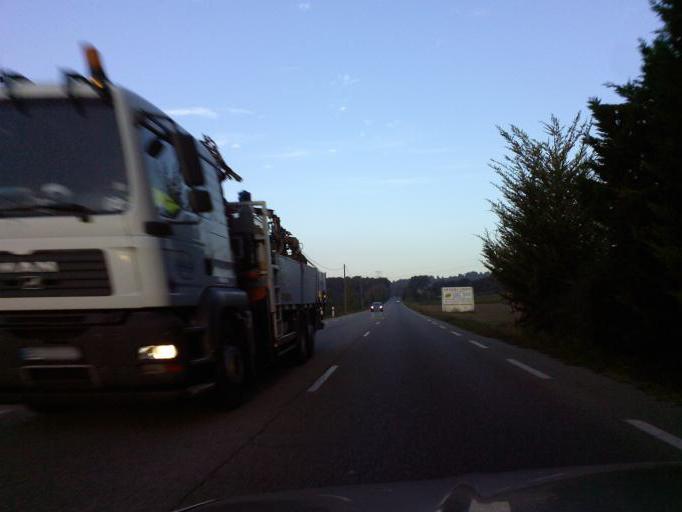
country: FR
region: Provence-Alpes-Cote d'Azur
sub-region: Departement des Bouches-du-Rhone
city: Lambesc
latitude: 43.6739
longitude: 5.2354
